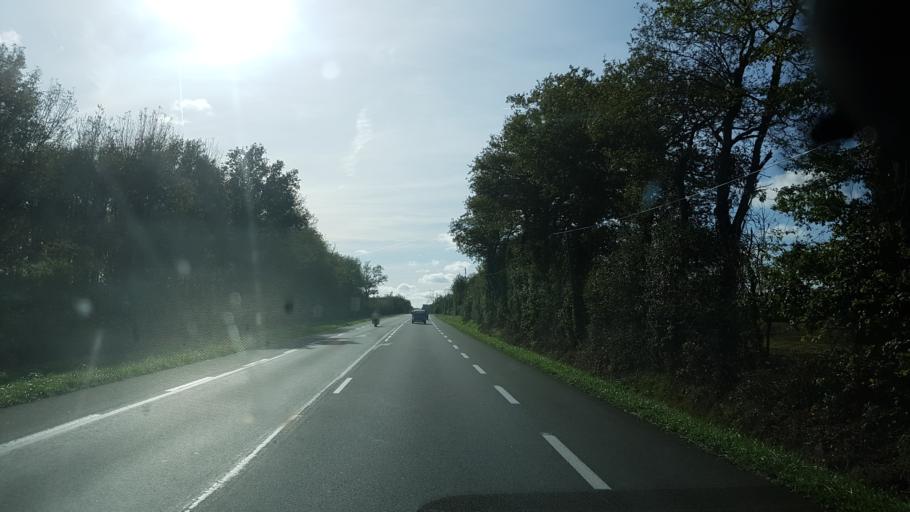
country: FR
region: Poitou-Charentes
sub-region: Departement de la Charente
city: Loubert
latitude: 45.9333
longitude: 0.5324
